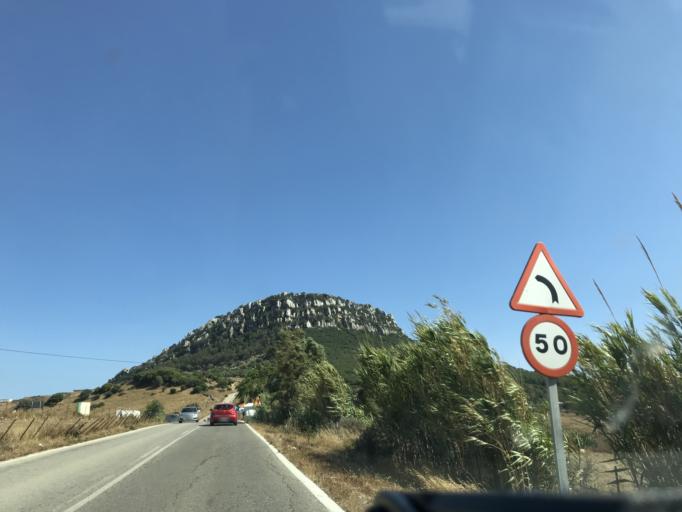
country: ES
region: Andalusia
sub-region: Provincia de Cadiz
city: Zahara de los Atunes
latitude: 36.1014
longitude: -5.7335
